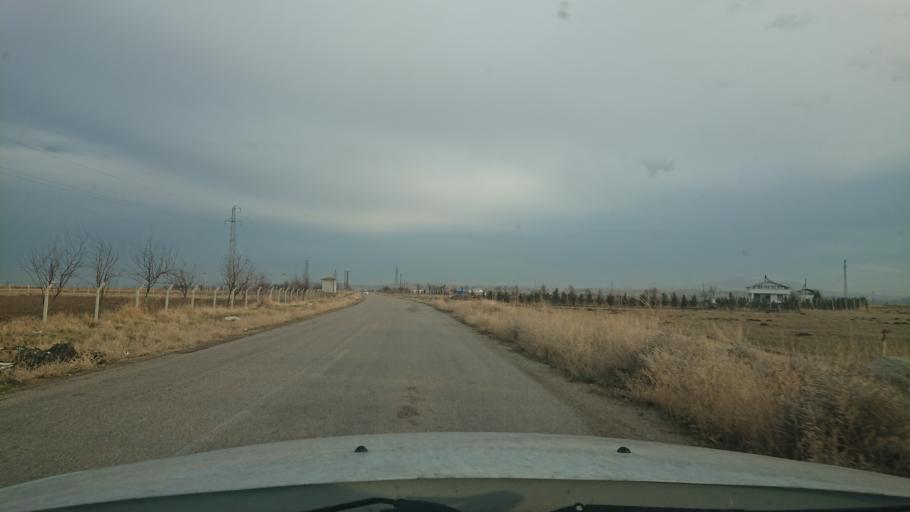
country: TR
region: Aksaray
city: Yesilova
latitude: 38.4253
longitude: 33.8353
